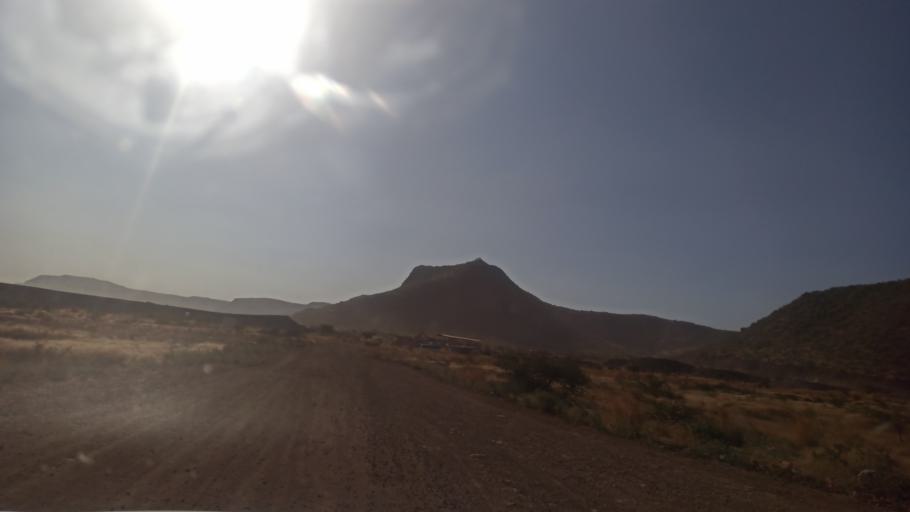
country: ET
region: Oromiya
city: Ziway
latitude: 7.9356
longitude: 38.6185
